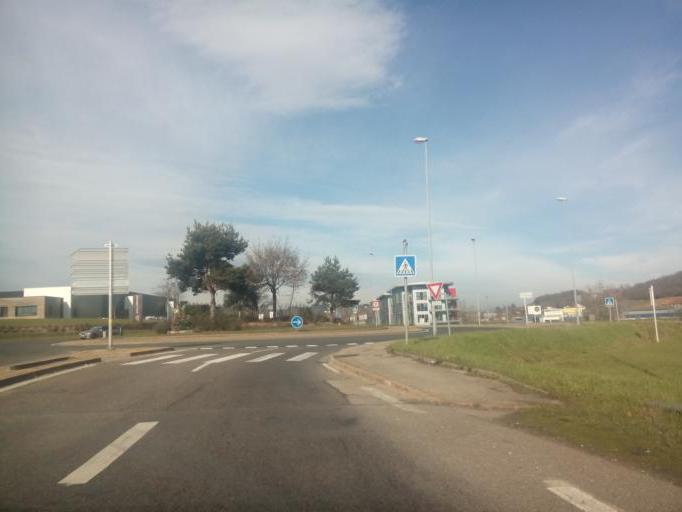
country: FR
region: Rhone-Alpes
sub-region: Departement du Rhone
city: Brignais
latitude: 45.6837
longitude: 4.7672
